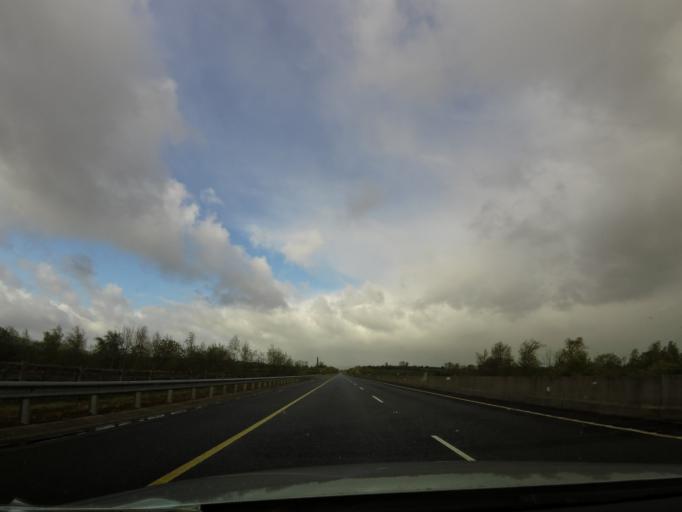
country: IE
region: Munster
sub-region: North Tipperary
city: Nenagh
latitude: 52.8464
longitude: -8.1914
